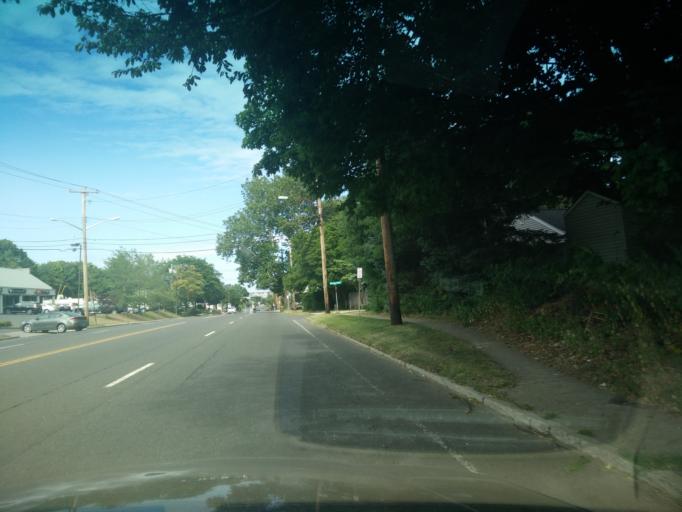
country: US
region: Connecticut
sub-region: Fairfield County
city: Fairfield
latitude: 41.1510
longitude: -73.2407
